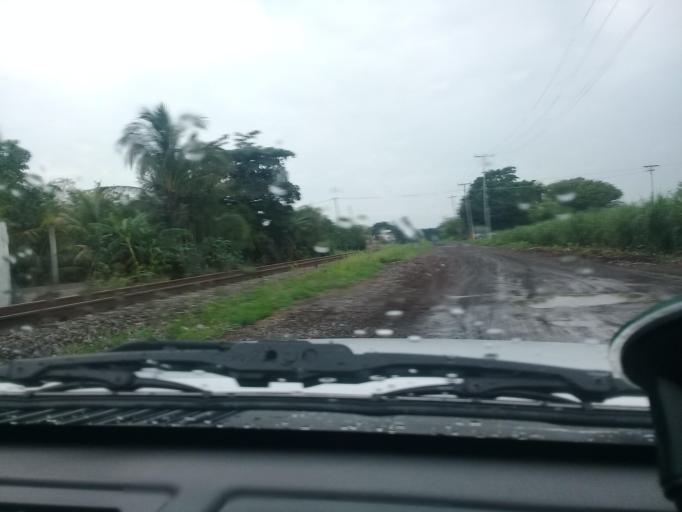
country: MX
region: Veracruz
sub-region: Puente Nacional
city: Cabezas
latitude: 19.3627
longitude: -96.4058
